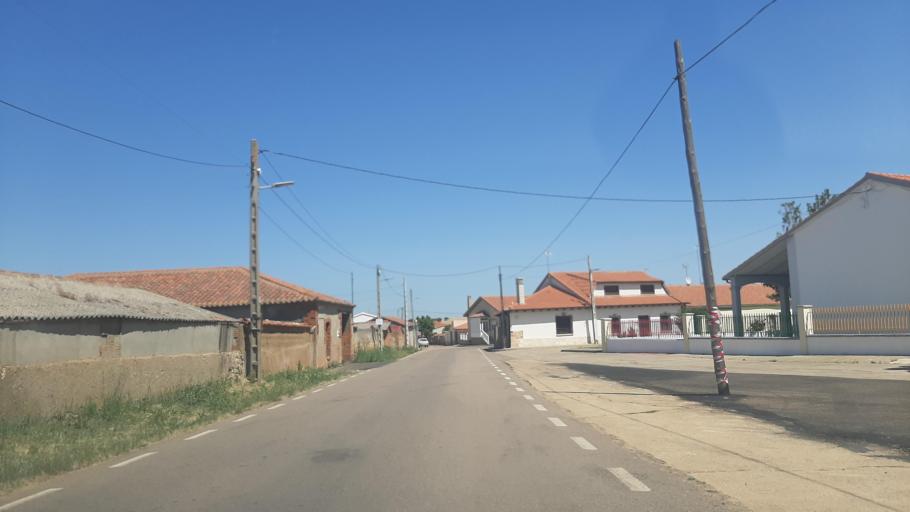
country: ES
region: Castille and Leon
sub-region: Provincia de Salamanca
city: Cabrillas
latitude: 40.7371
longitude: -6.1781
